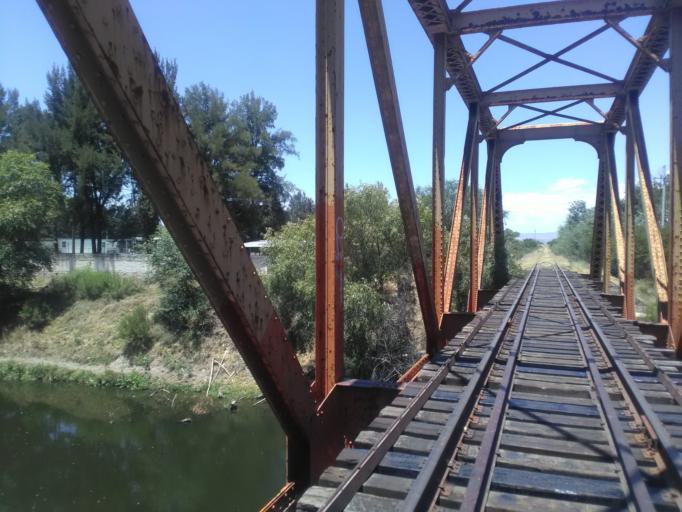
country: MX
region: Durango
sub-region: Durango
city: Jose Refugio Salcido
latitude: 24.0270
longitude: -104.5640
